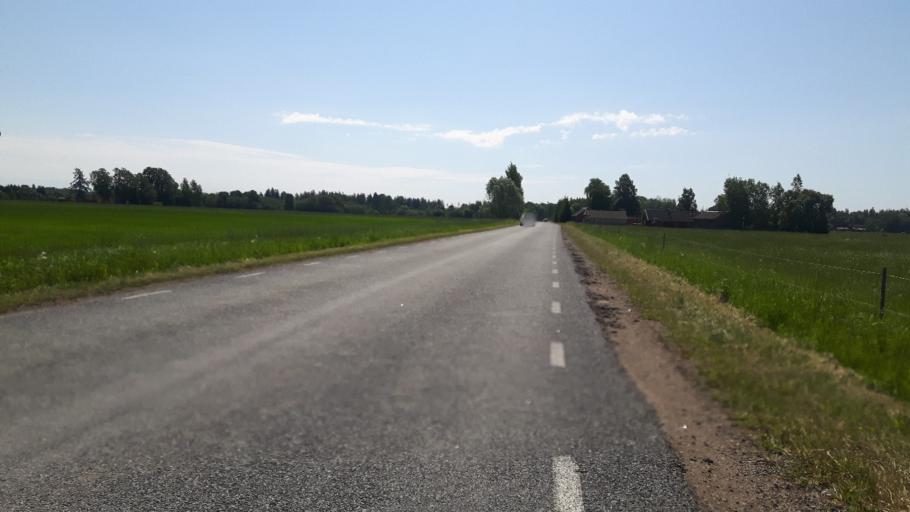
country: EE
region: Paernumaa
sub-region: Vaendra vald (alev)
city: Vandra
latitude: 58.5968
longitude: 25.0228
